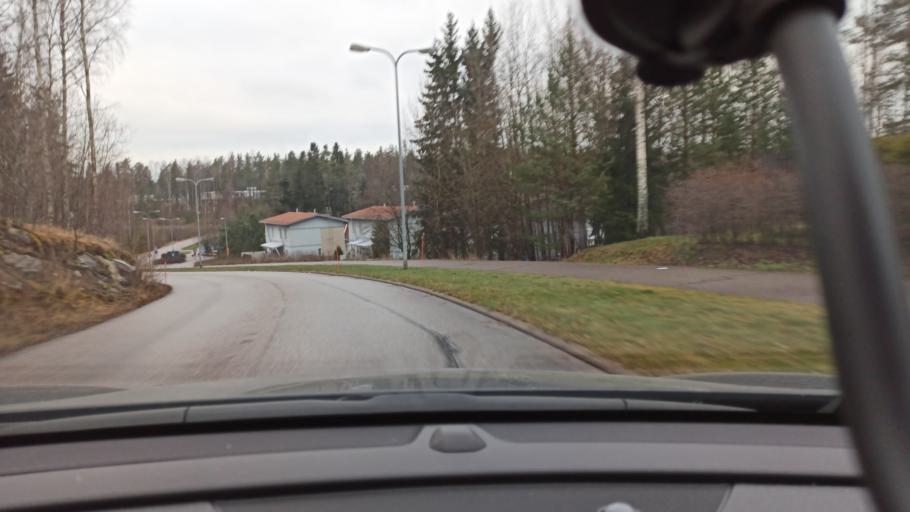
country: FI
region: Uusimaa
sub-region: Helsinki
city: Kirkkonummi
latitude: 60.1287
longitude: 24.4867
